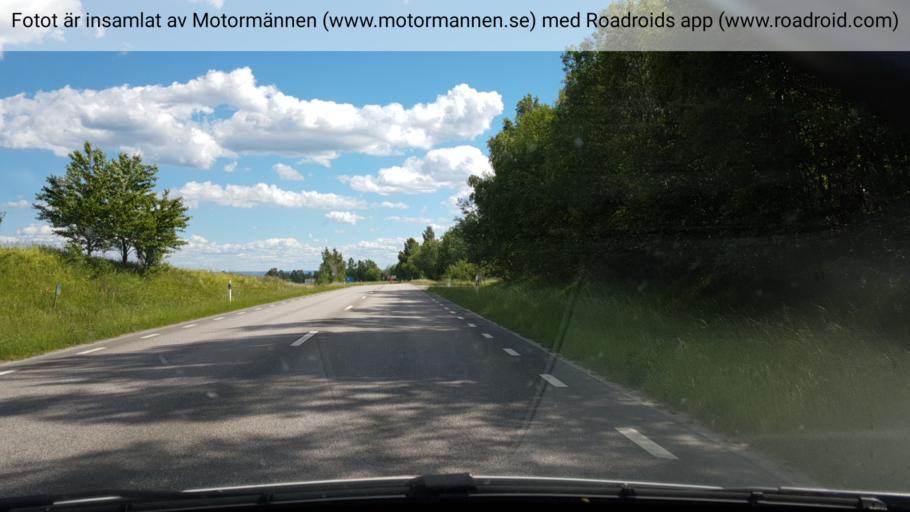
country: SE
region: Vaestra Goetaland
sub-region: Hjo Kommun
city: Hjo
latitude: 58.3265
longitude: 14.2591
